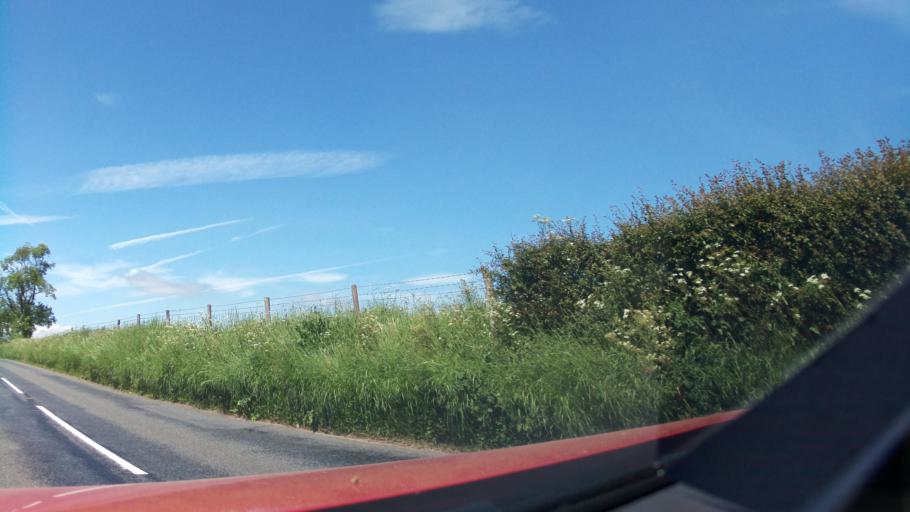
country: GB
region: Wales
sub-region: Monmouthshire
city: Caldicot
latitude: 51.6322
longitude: -2.7442
